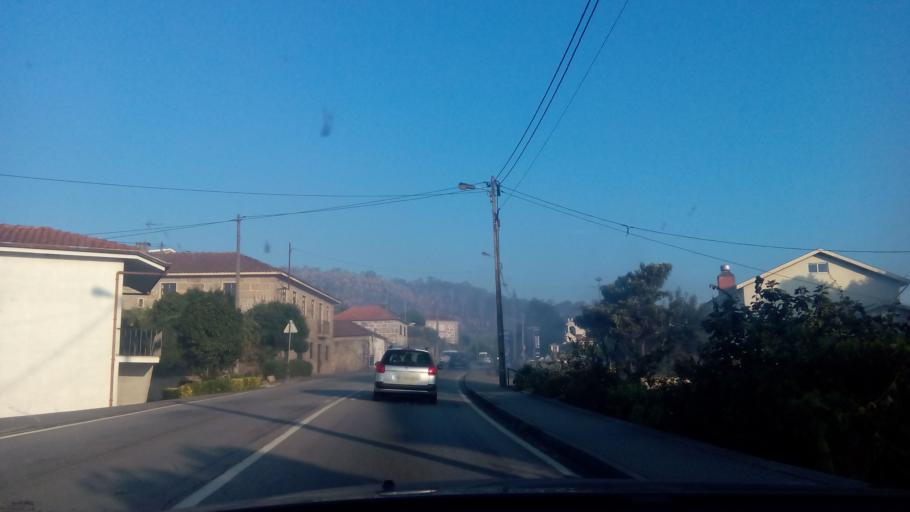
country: PT
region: Porto
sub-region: Paredes
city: Casteloes de Cepeda
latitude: 41.1977
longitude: -8.3534
